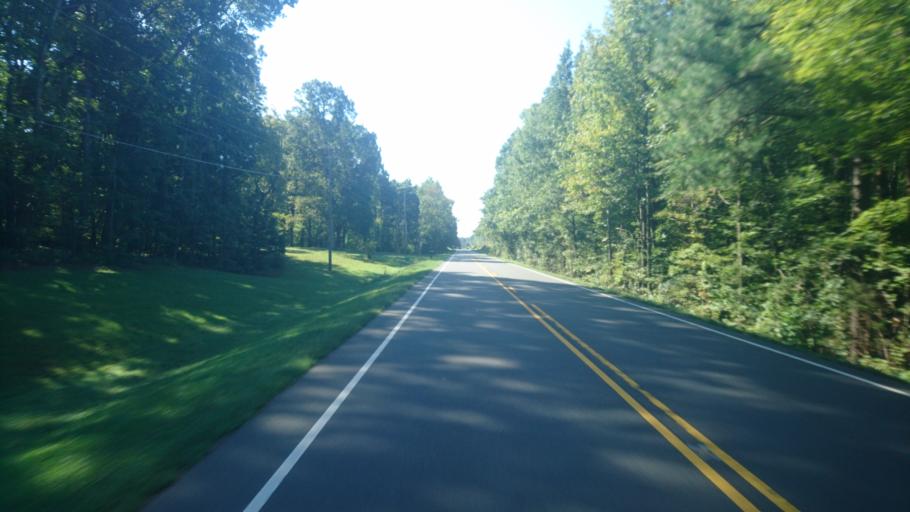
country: US
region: North Carolina
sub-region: Orange County
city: Hillsborough
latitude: 36.0342
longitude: -79.0814
